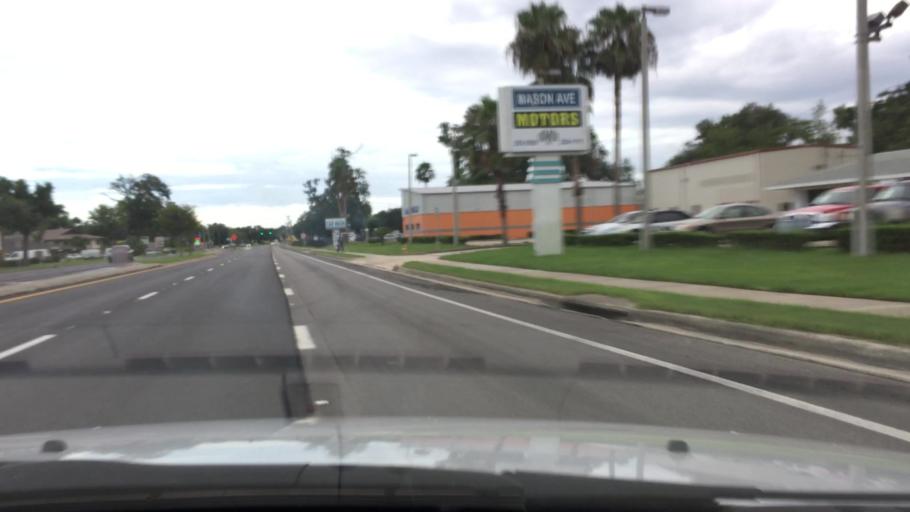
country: US
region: Florida
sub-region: Volusia County
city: Holly Hill
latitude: 29.2447
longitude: -81.0633
